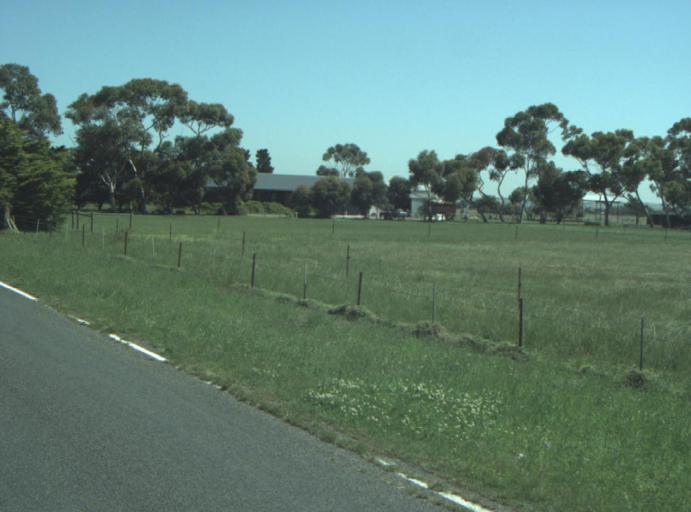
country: AU
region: Victoria
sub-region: Greater Geelong
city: Lara
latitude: -37.9921
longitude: 144.4019
